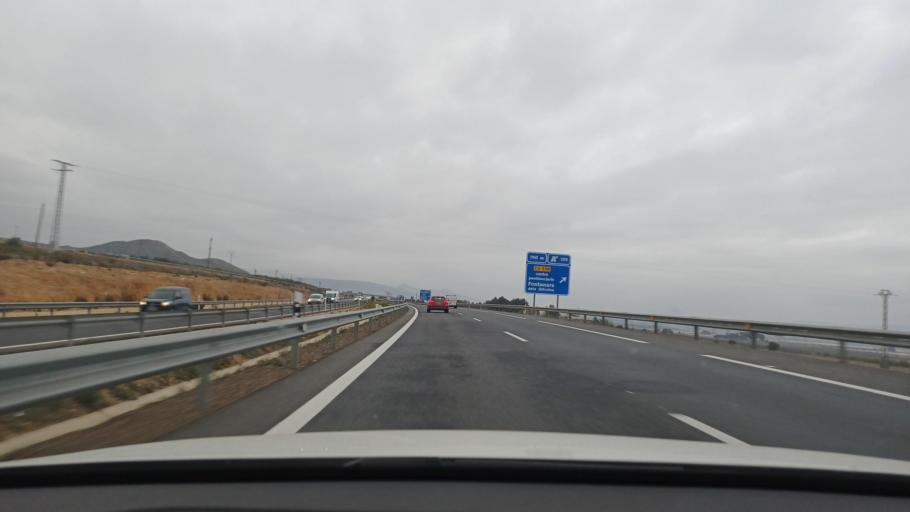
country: ES
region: Castille-La Mancha
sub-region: Provincia de Albacete
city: Caudete
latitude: 38.7036
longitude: -0.9242
